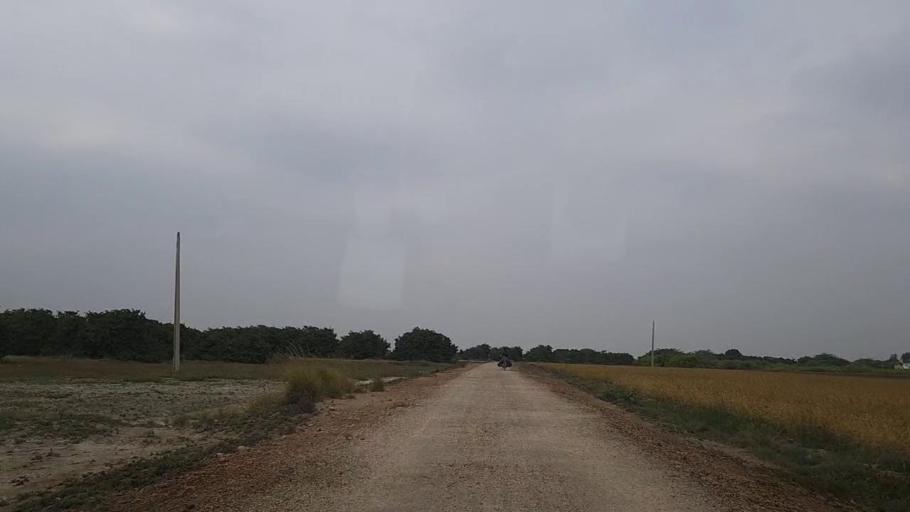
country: PK
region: Sindh
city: Mirpur Sakro
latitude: 24.6177
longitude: 67.7189
